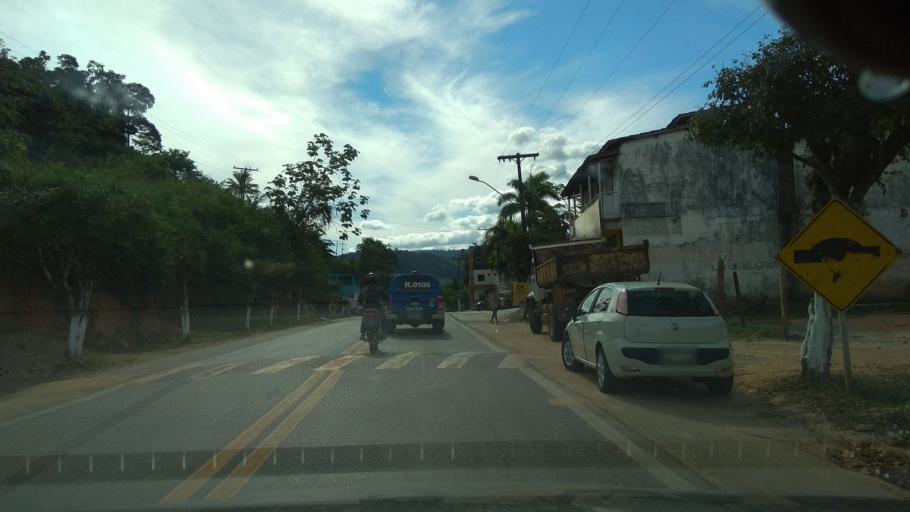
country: BR
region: Bahia
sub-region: Jitauna
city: Jitauna
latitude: -14.0143
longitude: -39.8917
